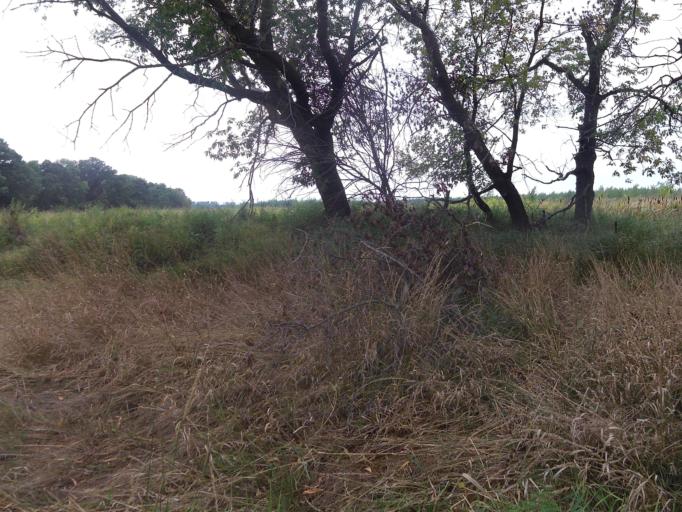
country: US
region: North Dakota
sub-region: Walsh County
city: Grafton
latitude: 48.4281
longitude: -97.1294
